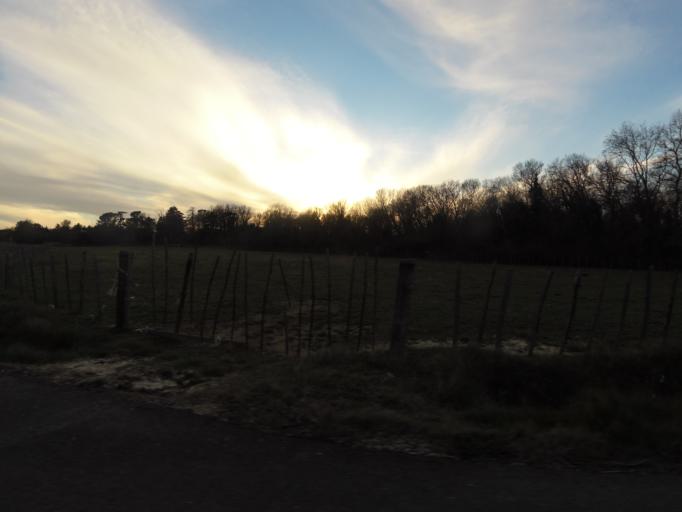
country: FR
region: Languedoc-Roussillon
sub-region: Departement du Gard
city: Saint-Mamert-du-Gard
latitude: 43.8641
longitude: 4.2149
